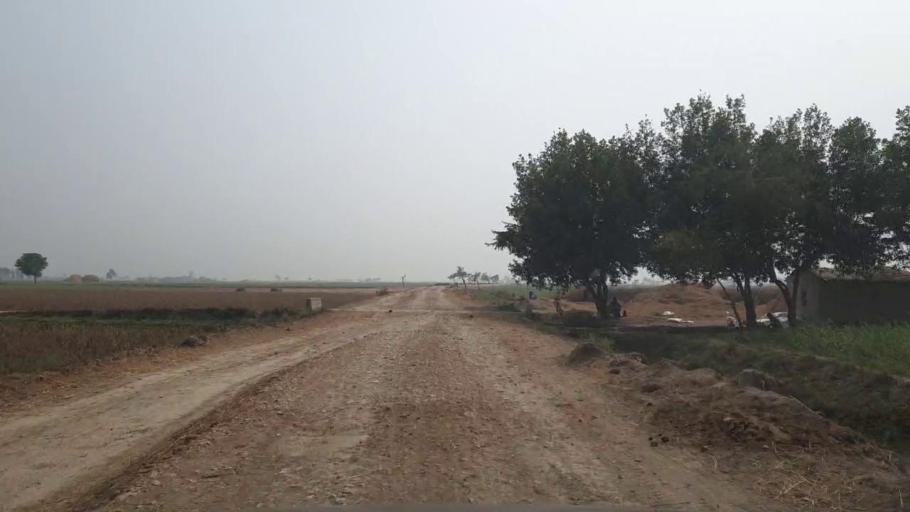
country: PK
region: Sindh
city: Kario
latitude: 24.6421
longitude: 68.5957
